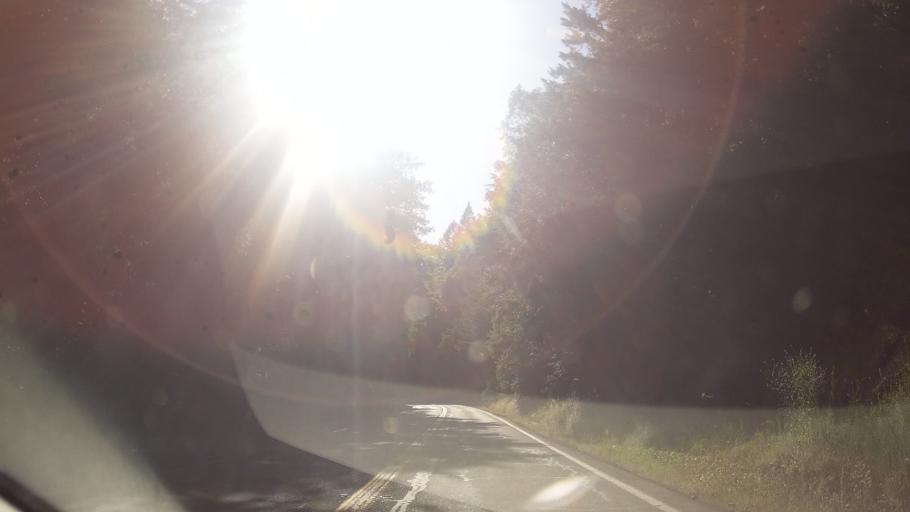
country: US
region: California
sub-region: Mendocino County
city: Brooktrails
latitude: 39.3880
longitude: -123.4381
